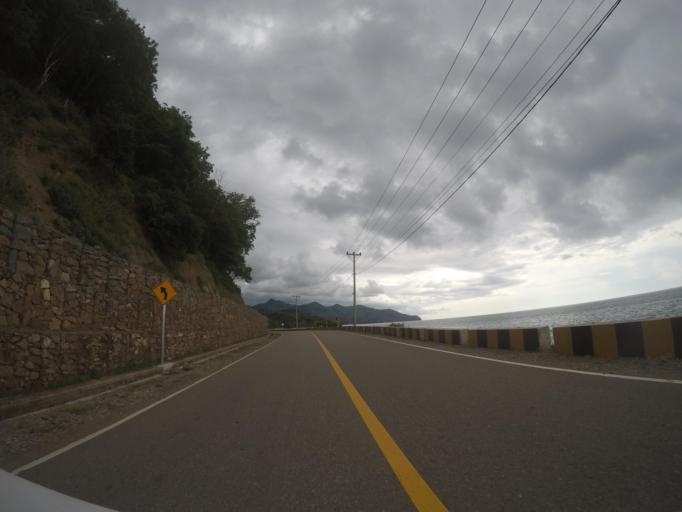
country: TL
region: Bobonaro
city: Maliana
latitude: -8.8127
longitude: 125.0826
